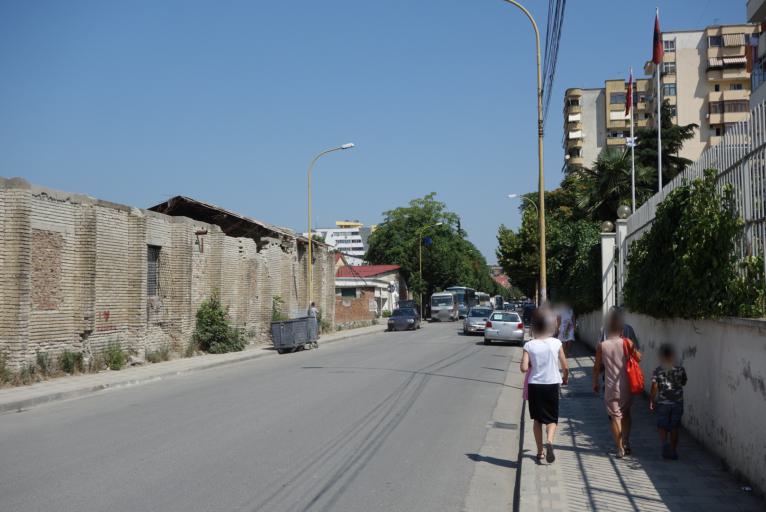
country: AL
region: Tirane
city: Tirana
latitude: 41.3211
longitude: 19.7989
